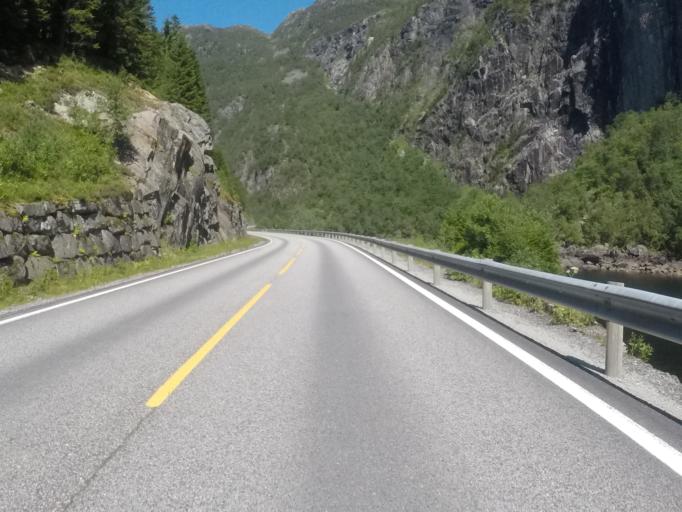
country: NO
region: Sogn og Fjordane
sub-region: Eid
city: Nordfjordeid
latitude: 61.9657
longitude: 6.1322
